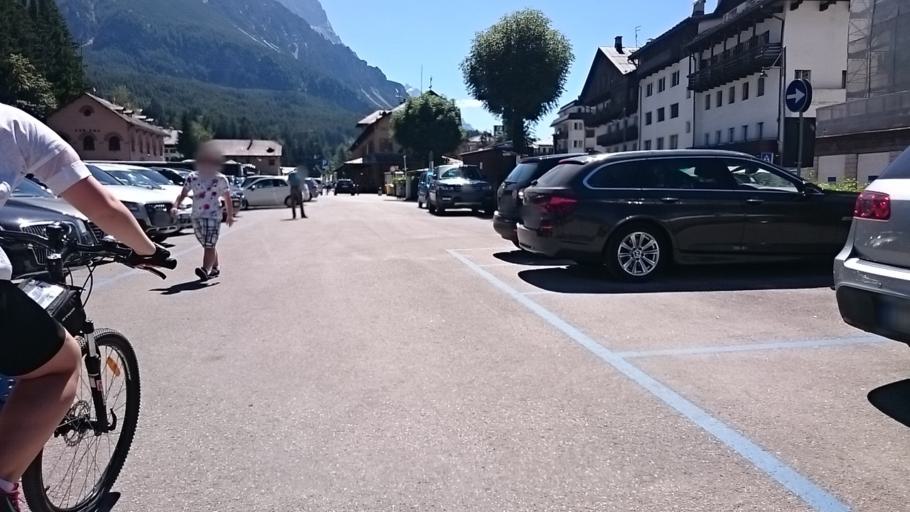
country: IT
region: Veneto
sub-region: Provincia di Belluno
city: Cortina d'Ampezzo
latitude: 46.5399
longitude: 12.1369
